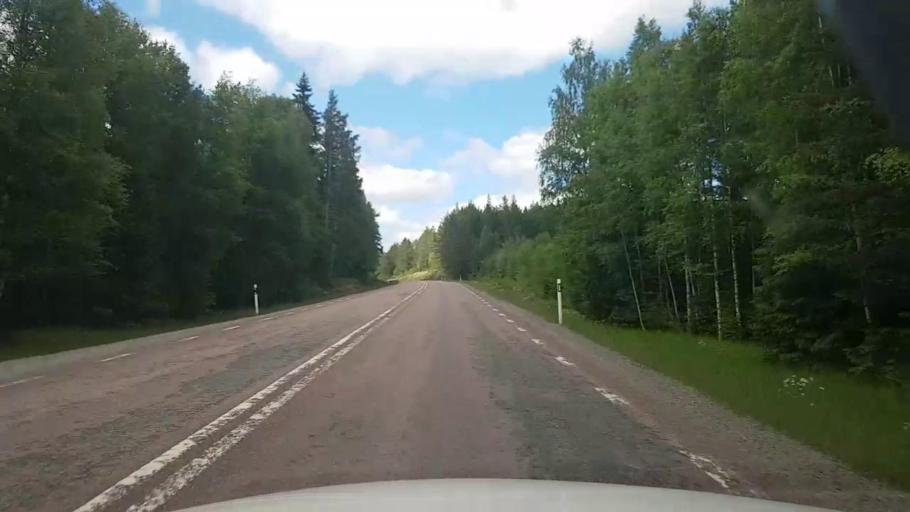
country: SE
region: Gaevleborg
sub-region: Ljusdals Kommun
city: Ljusdal
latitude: 61.7898
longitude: 16.1304
